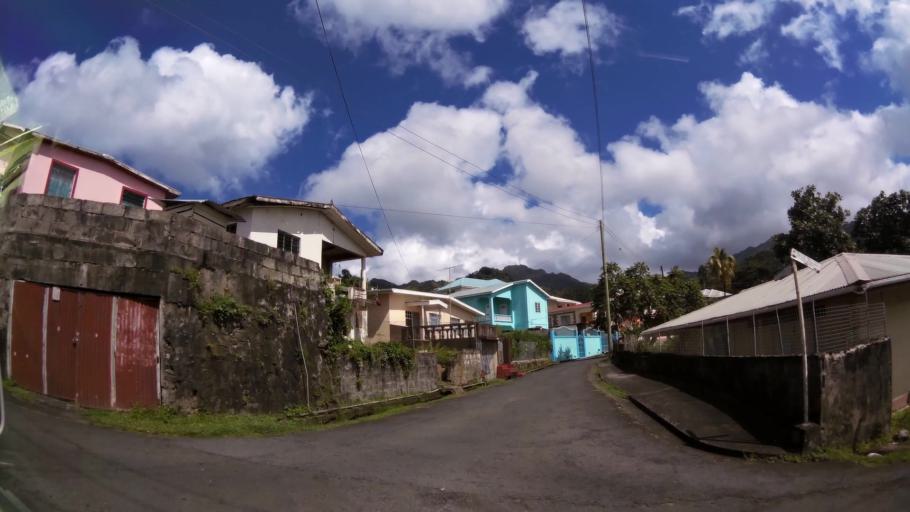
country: VC
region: Saint George
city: Kingstown
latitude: 13.1629
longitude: -61.2297
